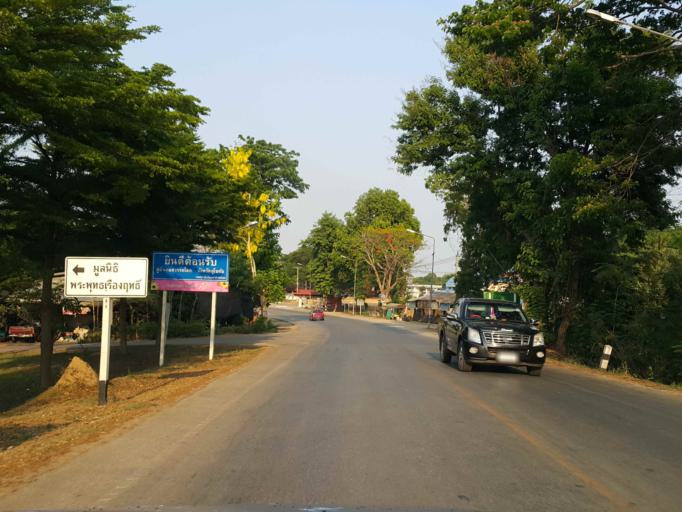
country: TH
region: Sukhothai
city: Sawankhalok
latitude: 17.3024
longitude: 99.8313
